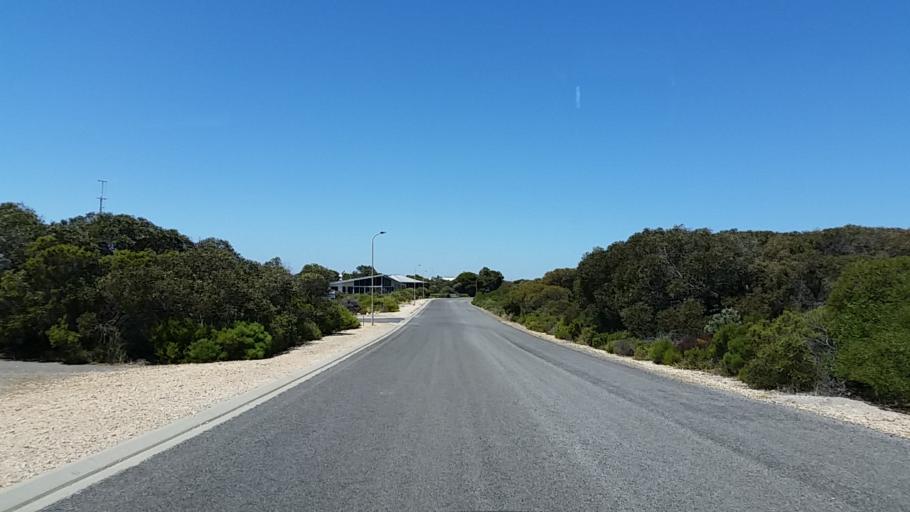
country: AU
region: South Australia
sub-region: Yorke Peninsula
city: Honiton
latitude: -35.2495
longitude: 136.9749
